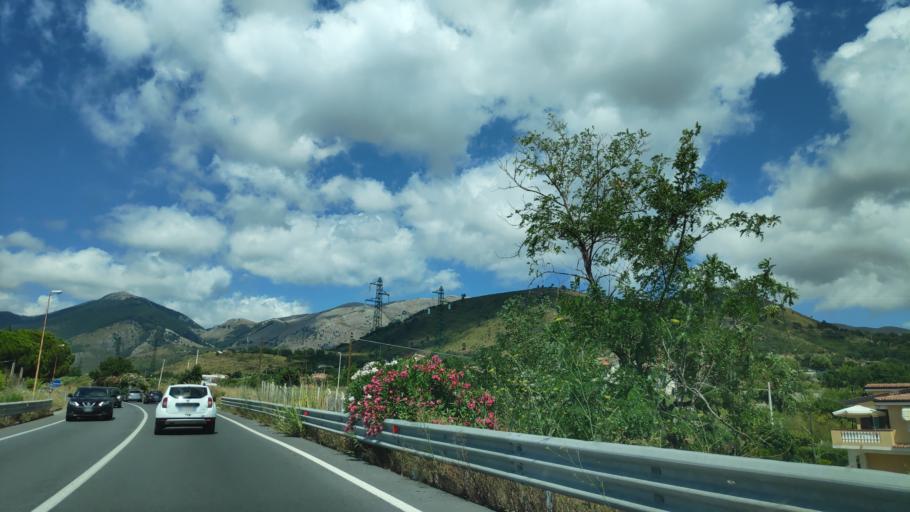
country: IT
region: Calabria
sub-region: Provincia di Cosenza
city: San Nicola Arcella
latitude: 39.8331
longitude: 15.7912
